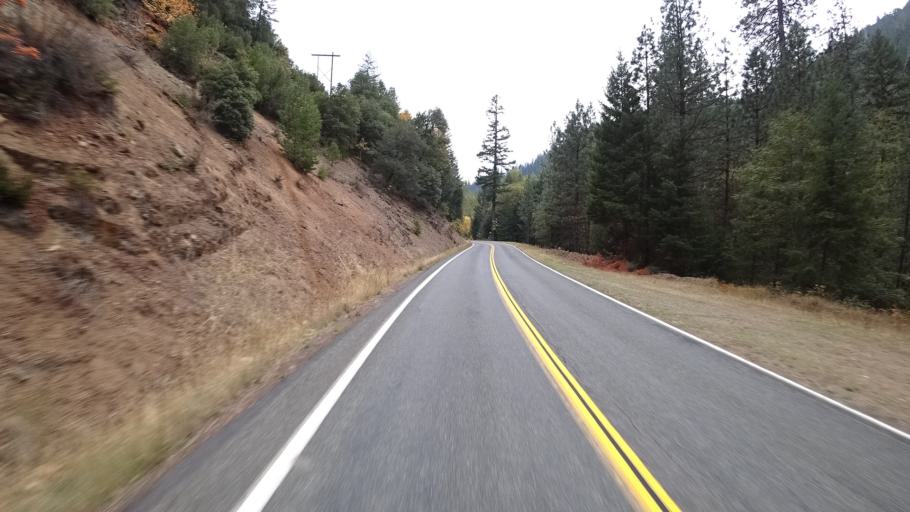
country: US
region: California
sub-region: Siskiyou County
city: Happy Camp
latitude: 41.8932
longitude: -123.4336
